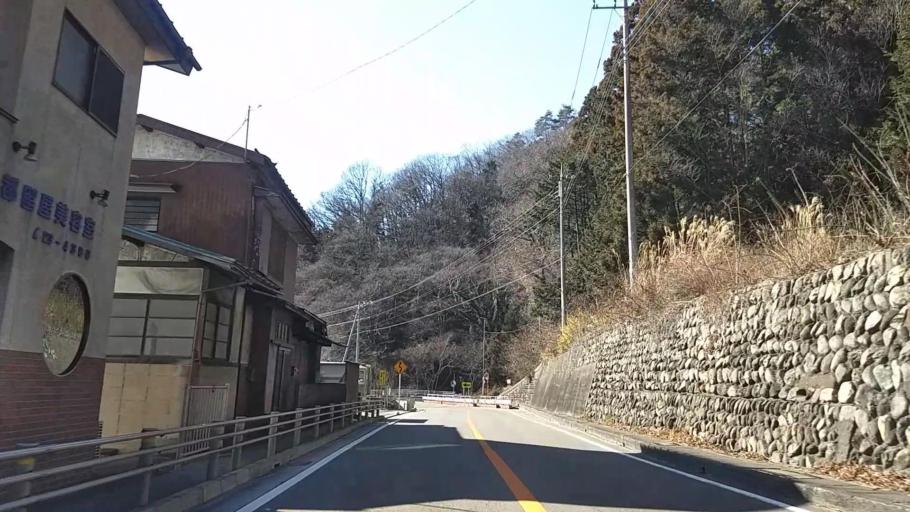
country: JP
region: Yamanashi
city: Otsuki
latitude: 35.6184
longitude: 138.9854
